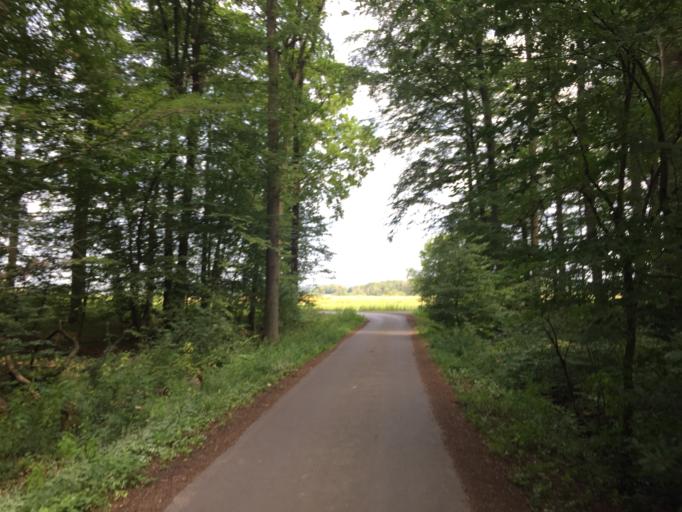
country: DE
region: Hesse
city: Staufenberg
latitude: 50.6483
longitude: 8.7507
